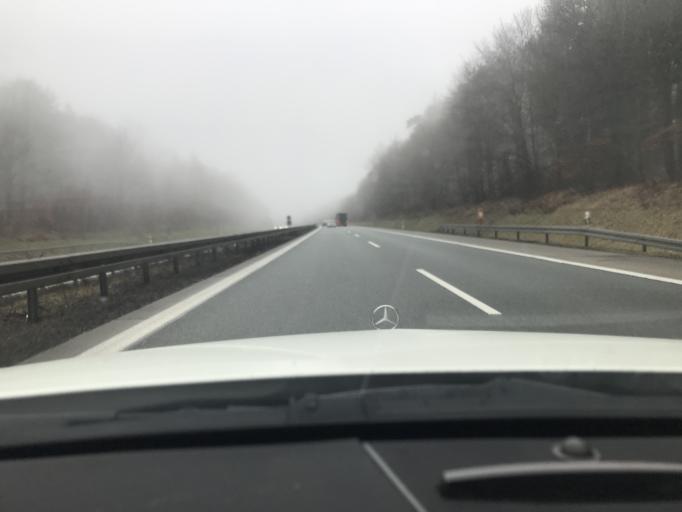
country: DE
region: Bavaria
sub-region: Regierungsbezirk Unterfranken
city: Schondra
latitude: 50.2217
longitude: 9.9012
